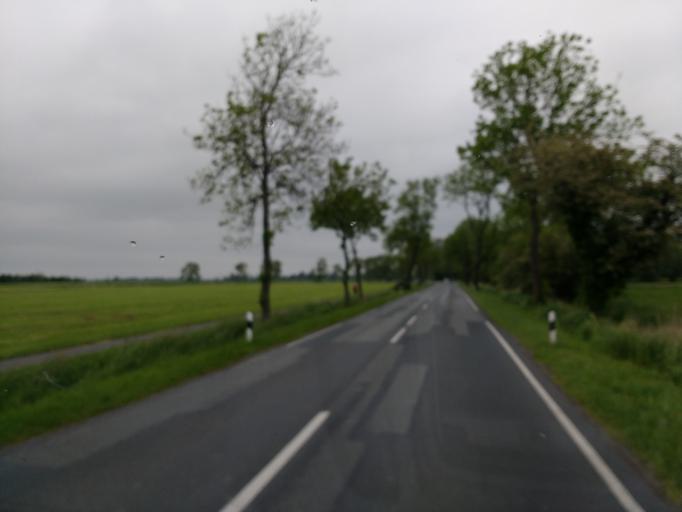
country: DE
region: Lower Saxony
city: Jever
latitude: 53.6142
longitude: 7.9326
